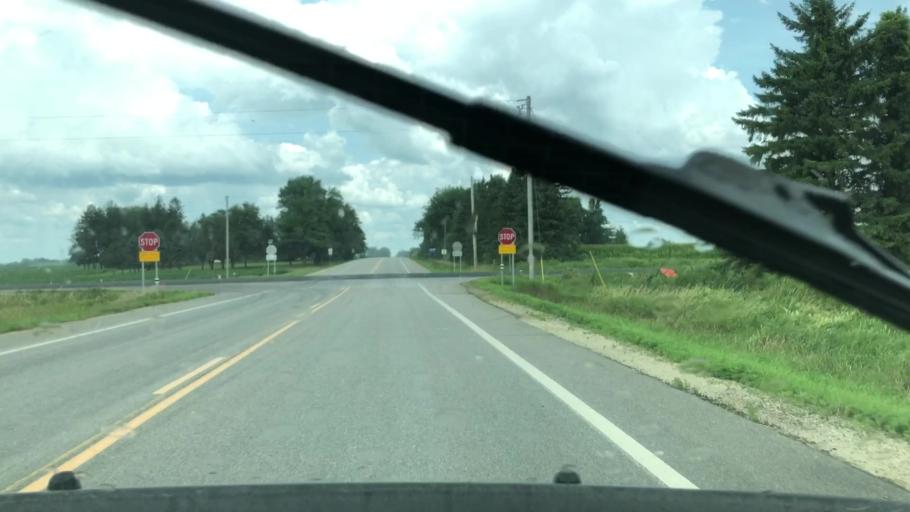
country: US
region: Minnesota
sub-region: Olmsted County
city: Stewartville
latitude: 43.8913
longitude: -92.5285
